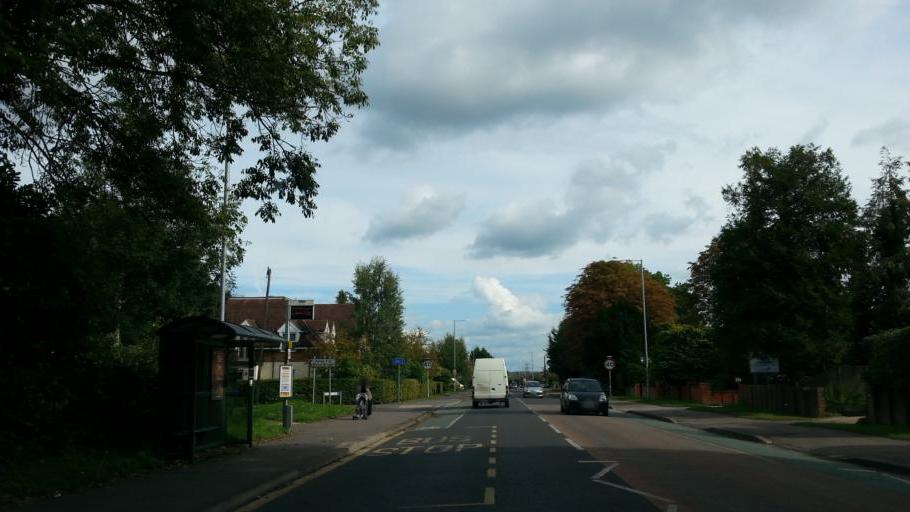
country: GB
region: England
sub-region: Wokingham
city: Earley
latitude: 51.4412
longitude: -0.9260
